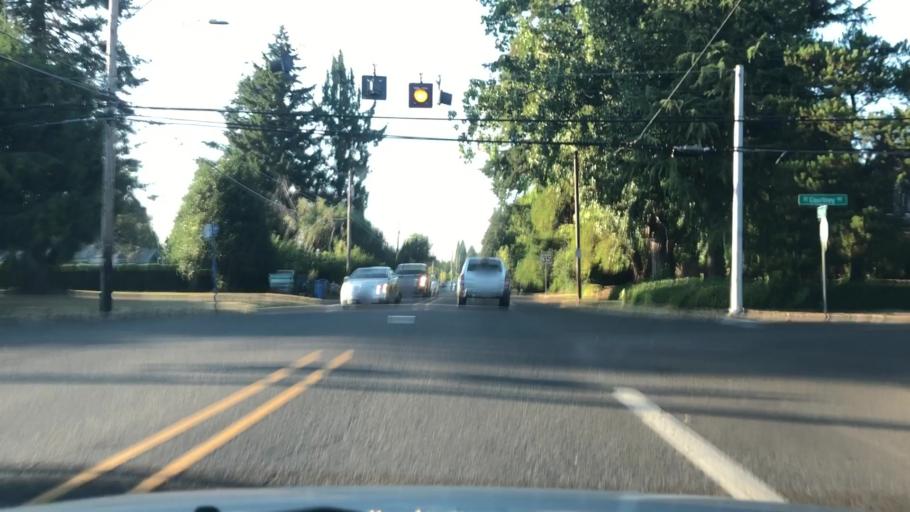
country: US
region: Oregon
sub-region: Clackamas County
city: Oak Grove
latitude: 45.4224
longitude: -122.6455
